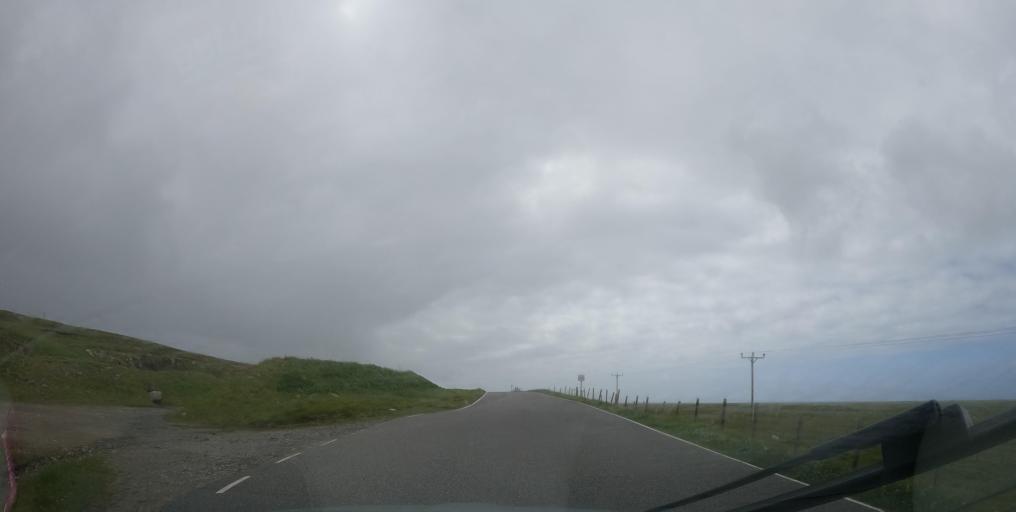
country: GB
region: Scotland
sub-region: Eilean Siar
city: Benbecula
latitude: 57.3461
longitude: -7.3621
